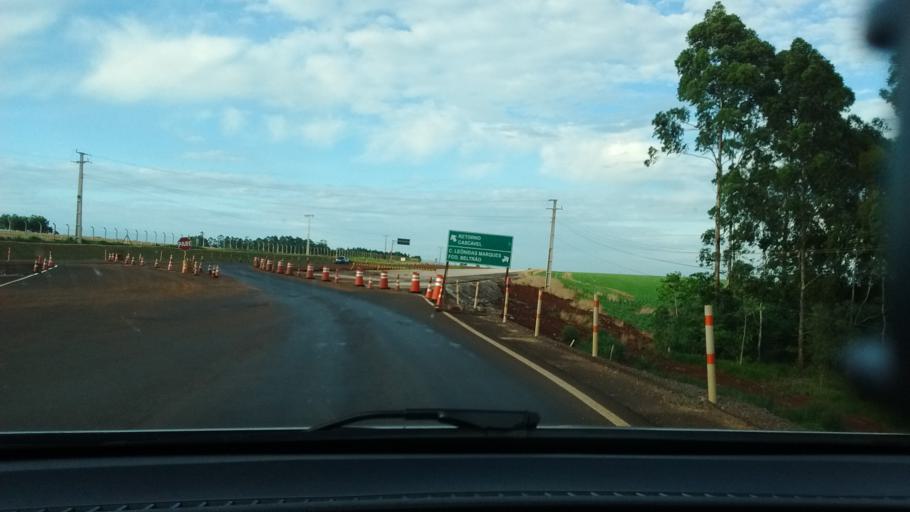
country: BR
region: Parana
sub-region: Cascavel
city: Cascavel
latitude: -25.0828
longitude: -53.5860
